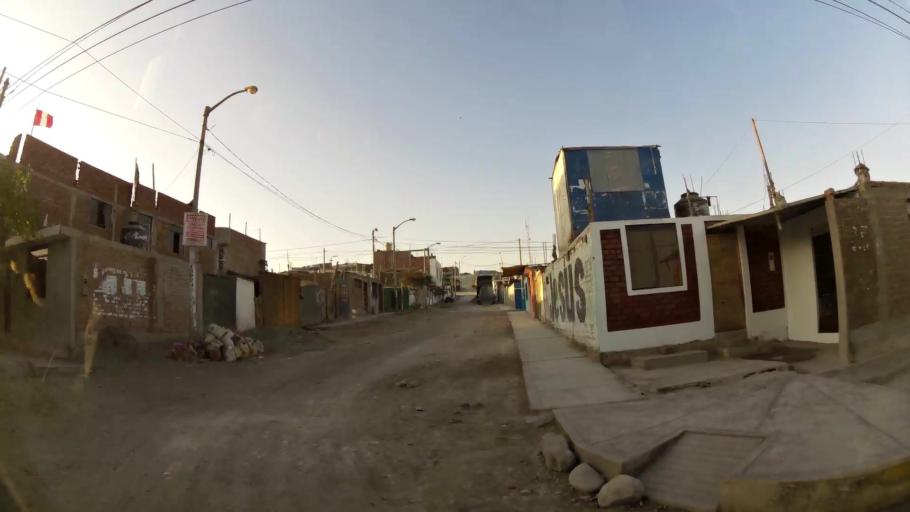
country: PE
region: Ica
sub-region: Provincia de Pisco
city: Villa Tupac Amaru
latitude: -13.7017
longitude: -76.1559
